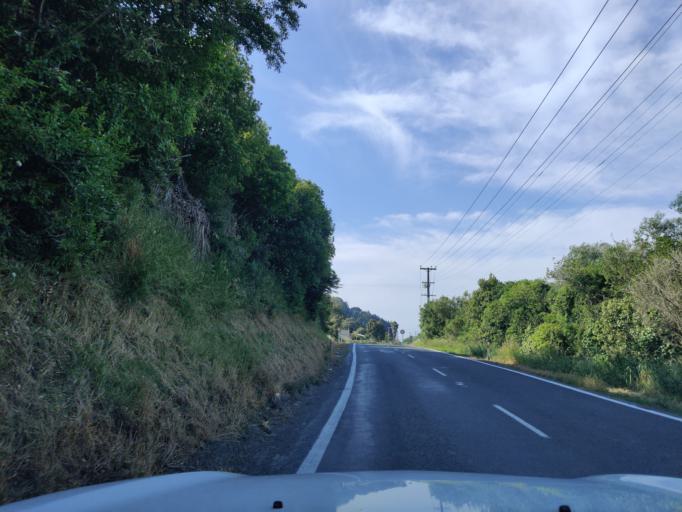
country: NZ
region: Waikato
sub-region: Waikato District
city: Ngaruawahia
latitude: -37.5847
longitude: 175.1544
